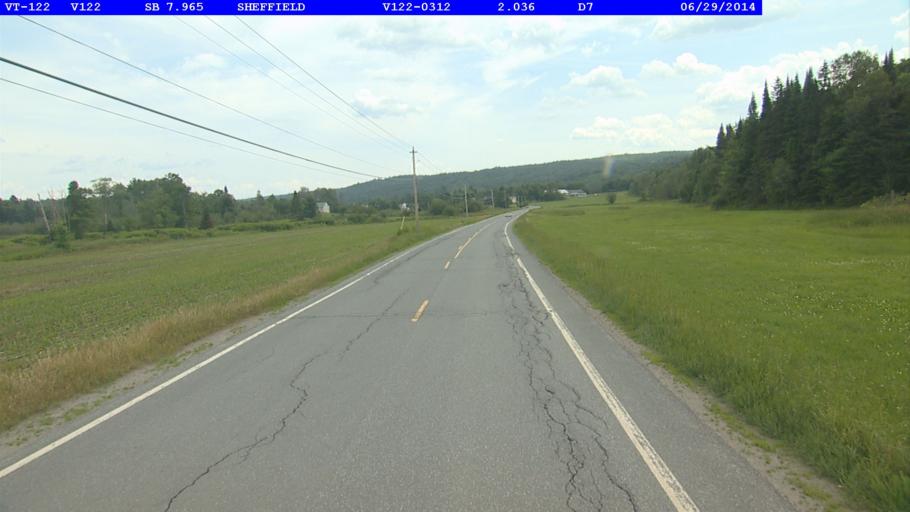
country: US
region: Vermont
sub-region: Caledonia County
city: Lyndonville
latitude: 44.6092
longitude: -72.1207
